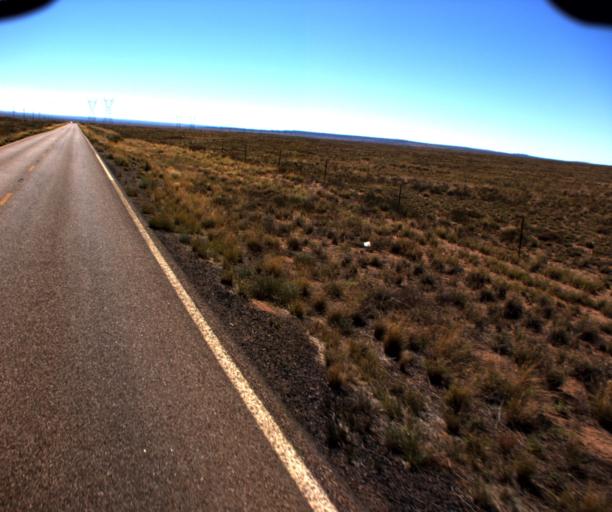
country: US
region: Arizona
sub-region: Navajo County
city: Holbrook
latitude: 35.1683
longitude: -110.0787
